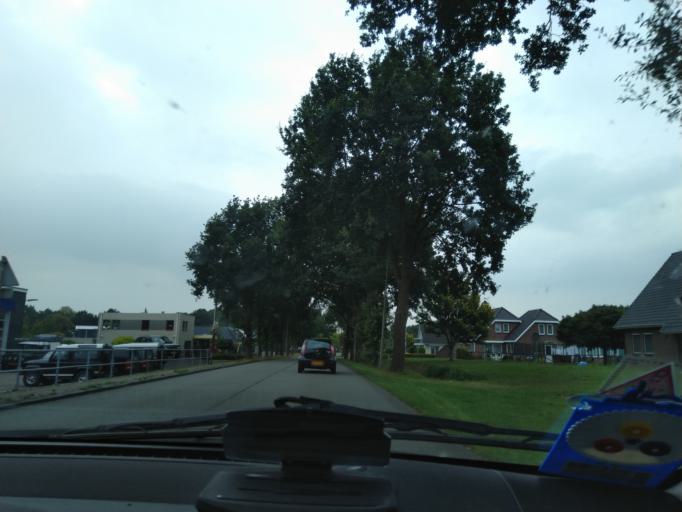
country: NL
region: Groningen
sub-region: Gemeente Pekela
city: Oude Pekela
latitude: 53.1126
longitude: 7.0254
